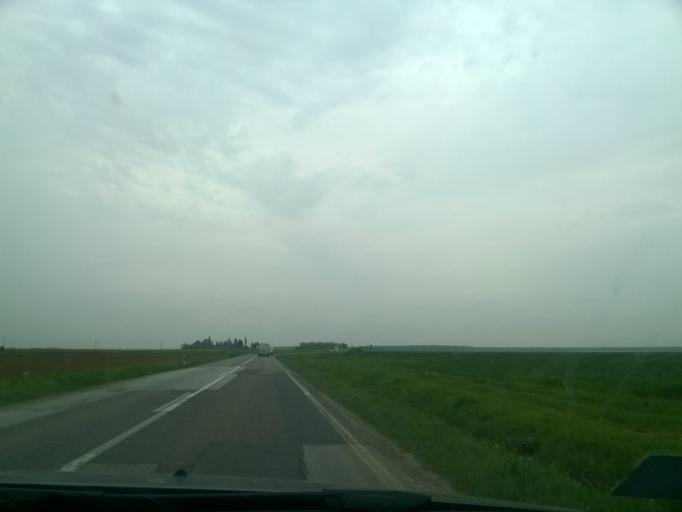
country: RS
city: Hrtkovci
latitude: 44.8634
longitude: 19.7717
